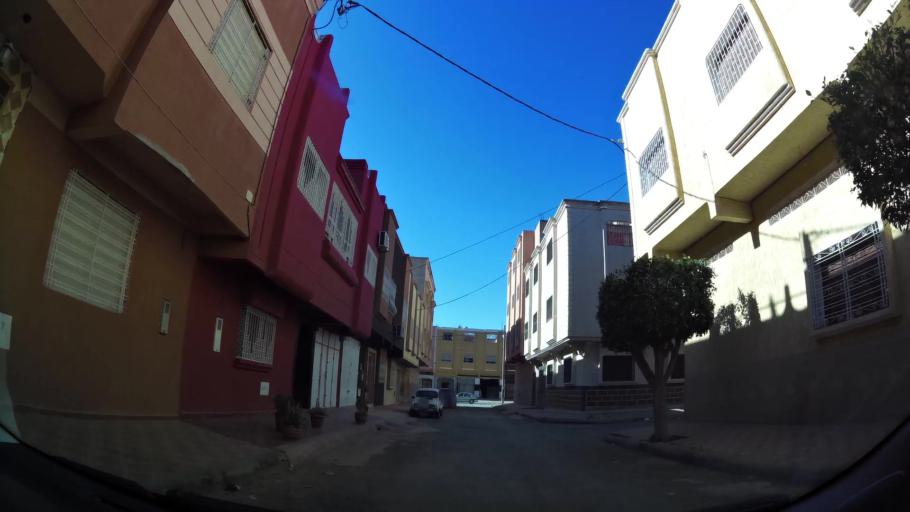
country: MA
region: Oriental
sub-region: Berkane-Taourirt
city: Berkane
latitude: 34.9359
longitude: -2.3334
